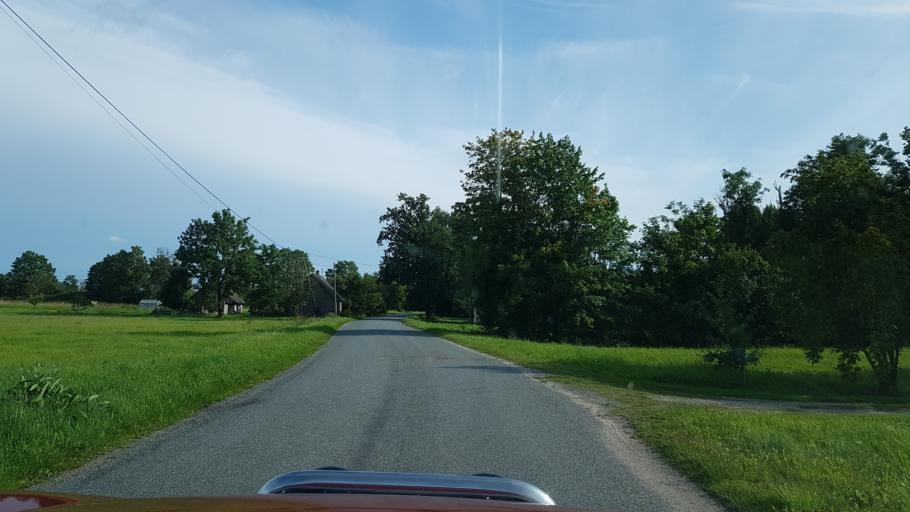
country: EE
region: Laeaene
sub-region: Lihula vald
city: Lihula
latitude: 58.4467
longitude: 24.0020
